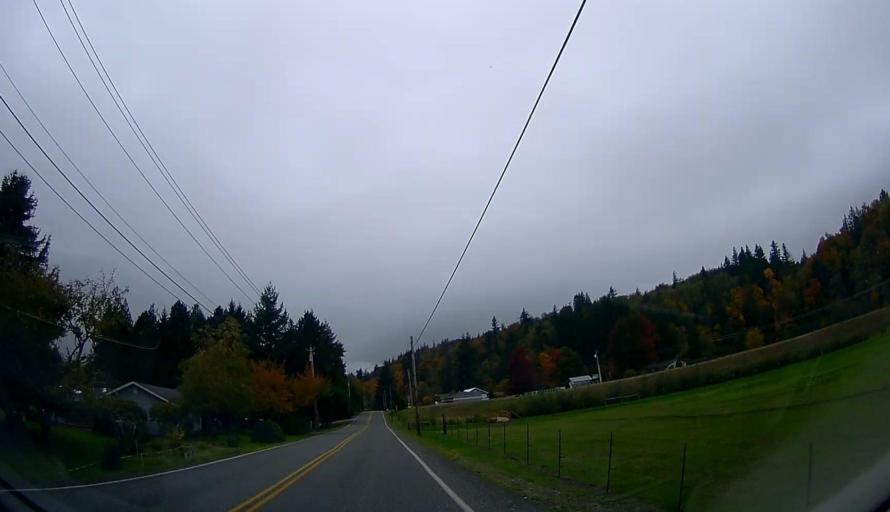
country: US
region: Washington
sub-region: Skagit County
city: Sedro-Woolley
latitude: 48.5273
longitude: -122.0993
